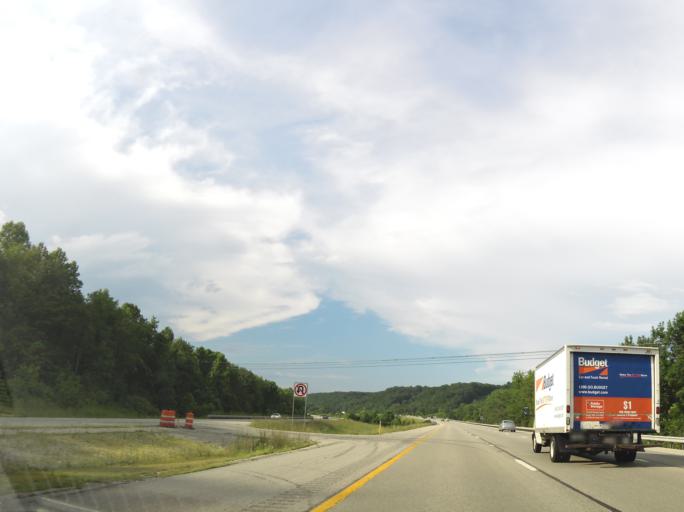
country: US
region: Kentucky
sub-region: Madison County
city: Berea
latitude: 37.5159
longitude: -84.3205
